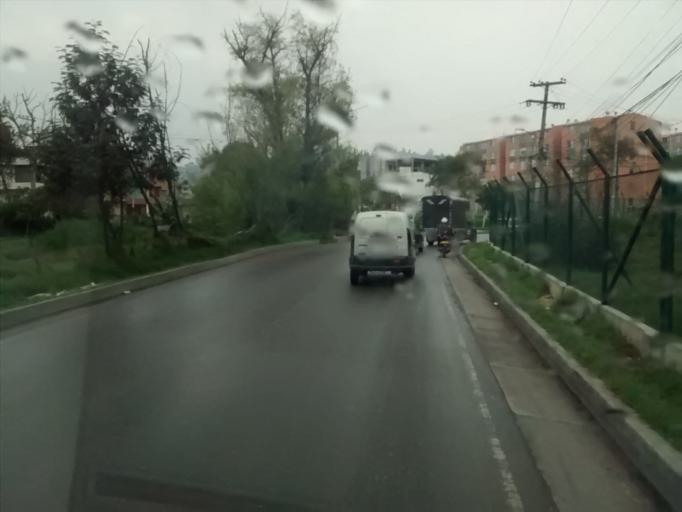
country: CO
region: Cundinamarca
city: Cota
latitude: 4.7584
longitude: -74.0922
